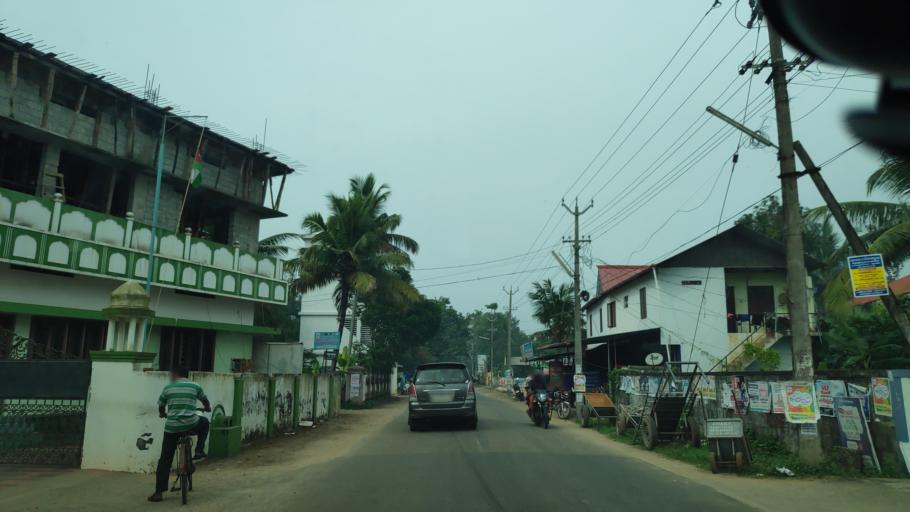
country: IN
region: Kerala
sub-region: Alappuzha
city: Alleppey
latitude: 9.5722
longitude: 76.3416
